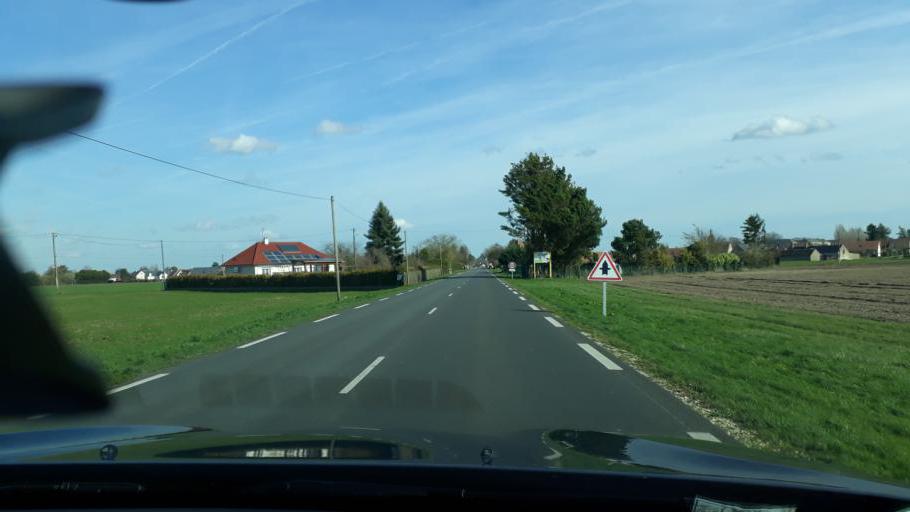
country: FR
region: Centre
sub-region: Departement du Loiret
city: Neuville-aux-Bois
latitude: 48.0684
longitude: 2.0383
